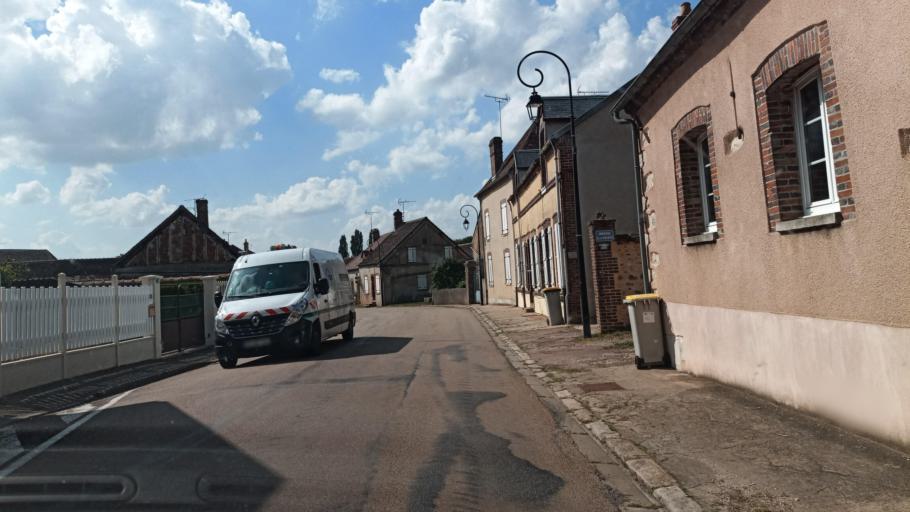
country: FR
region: Bourgogne
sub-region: Departement de l'Yonne
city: Egriselles-le-Bocage
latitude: 48.0555
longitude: 3.1472
